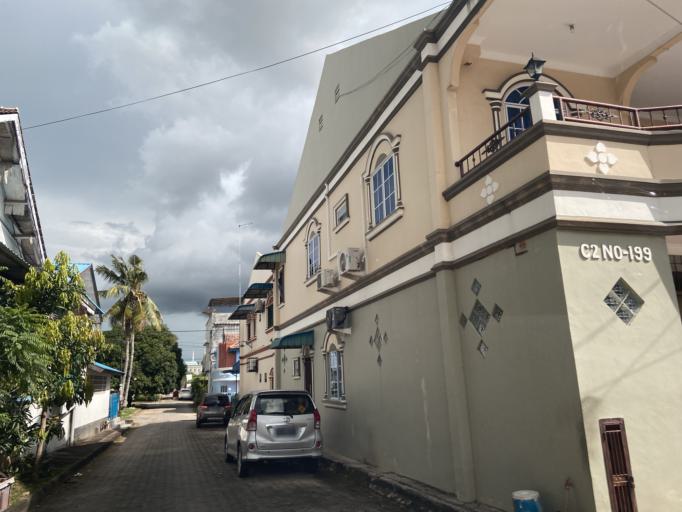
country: SG
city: Singapore
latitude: 1.1213
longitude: 104.0247
